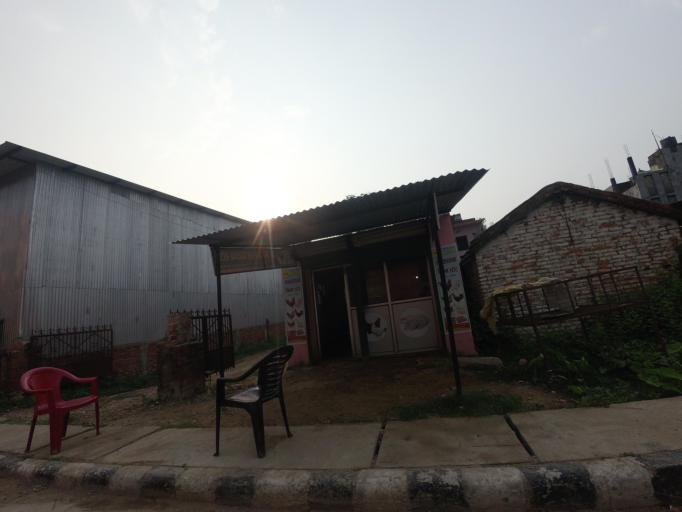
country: NP
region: Western Region
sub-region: Lumbini Zone
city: Bhairahawa
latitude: 27.5020
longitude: 83.4488
